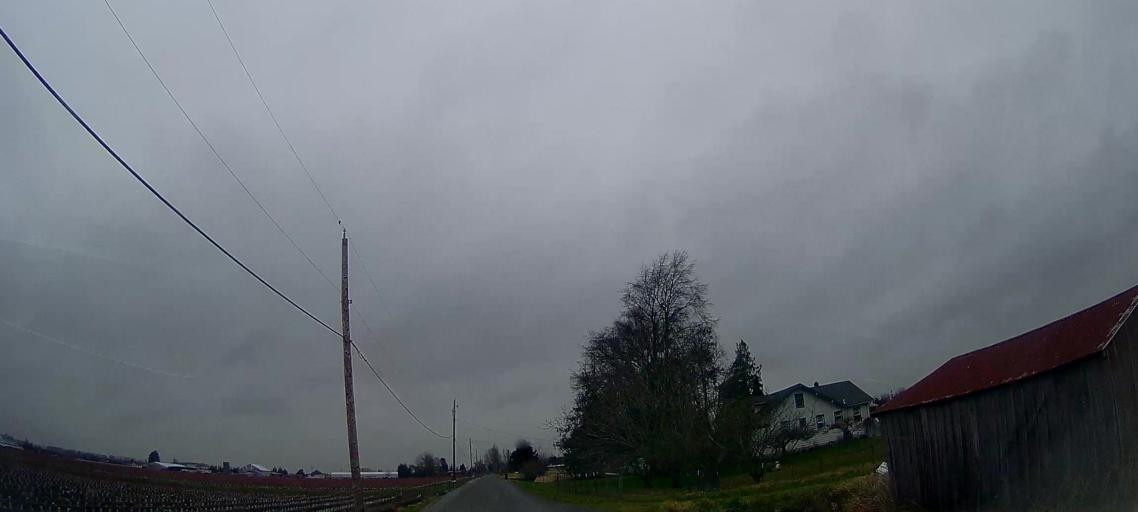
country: US
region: Washington
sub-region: Skagit County
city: Mount Vernon
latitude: 48.3704
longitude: -122.3174
